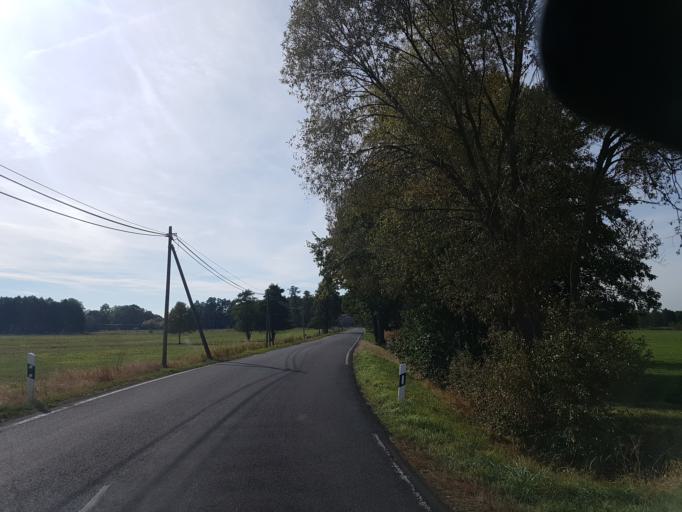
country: DE
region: Brandenburg
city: Schlieben
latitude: 51.7091
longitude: 13.4109
